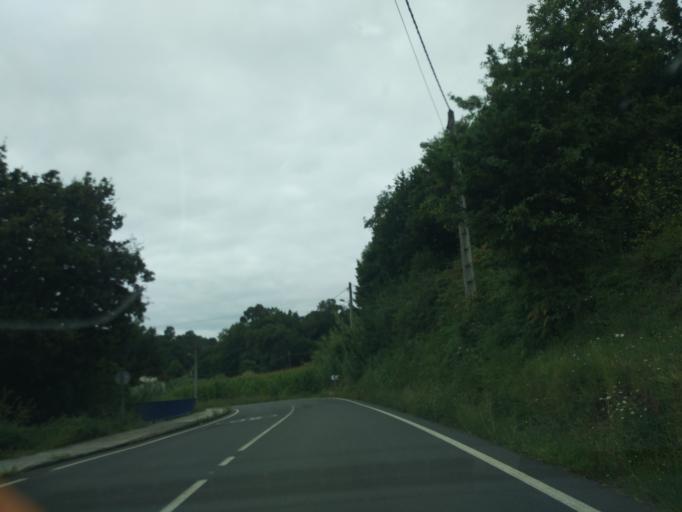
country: ES
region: Galicia
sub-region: Provincia da Coruna
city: Boiro
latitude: 42.6476
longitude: -8.8609
